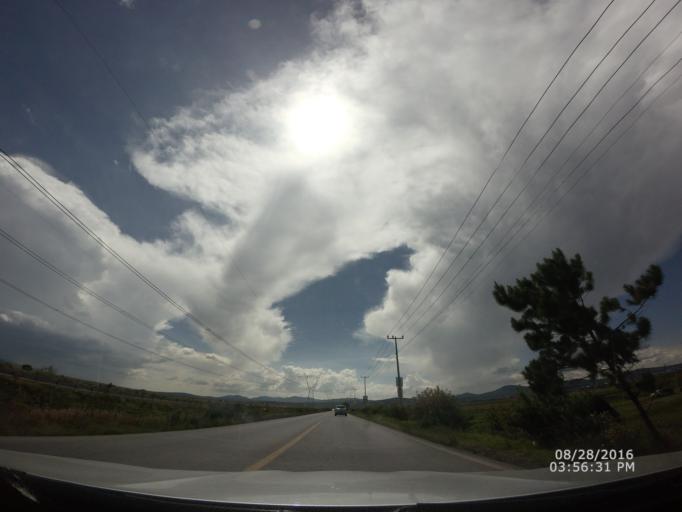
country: MX
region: Hidalgo
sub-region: Mineral de la Reforma
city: Los Tuzos
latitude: 20.0359
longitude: -98.7568
